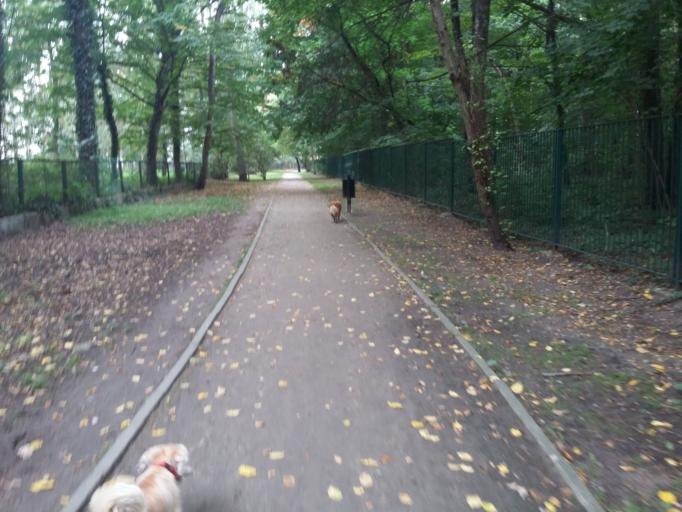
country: PL
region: Lodz Voivodeship
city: Lodz
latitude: 51.7581
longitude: 19.4208
